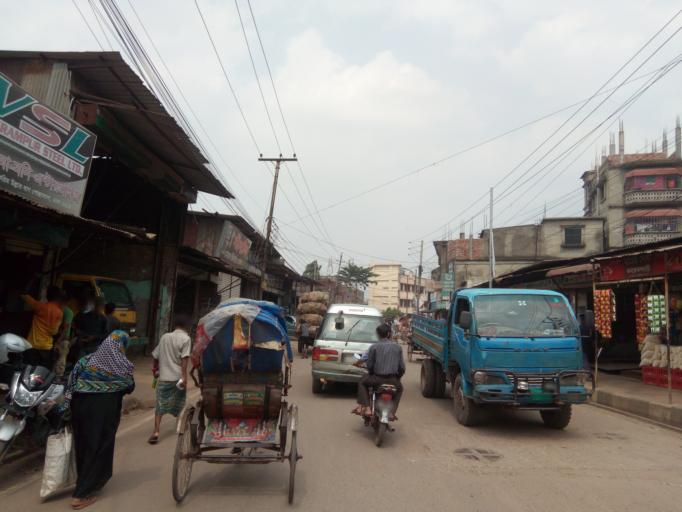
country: BD
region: Dhaka
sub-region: Dhaka
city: Dhaka
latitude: 23.6933
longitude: 90.4275
